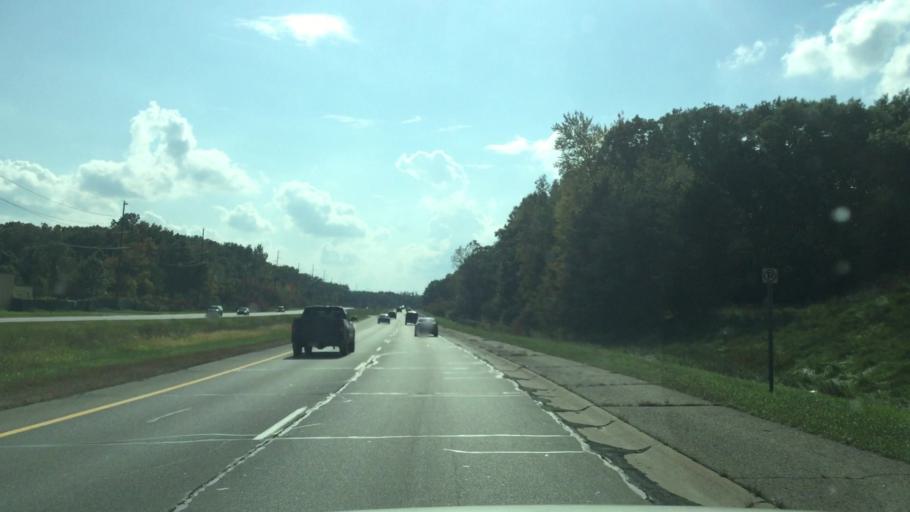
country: US
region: Michigan
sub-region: Oakland County
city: Milford
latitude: 42.6511
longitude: -83.5927
